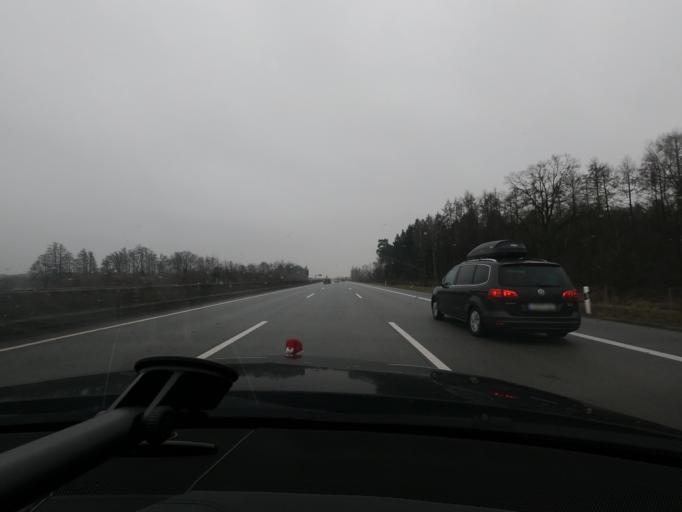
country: DE
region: Schleswig-Holstein
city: Grossenaspe
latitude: 53.9946
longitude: 9.9370
